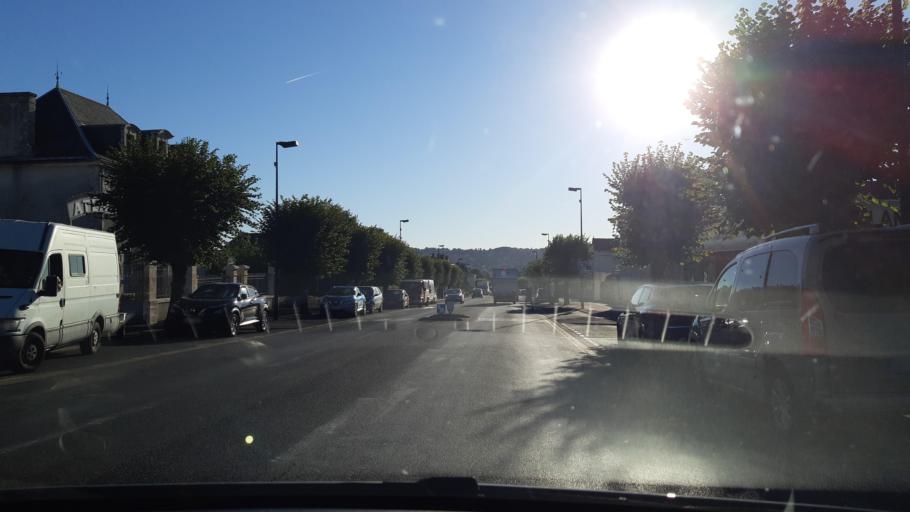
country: FR
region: Poitou-Charentes
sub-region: Departement des Deux-Sevres
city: Exireuil
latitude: 46.4113
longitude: -0.2124
